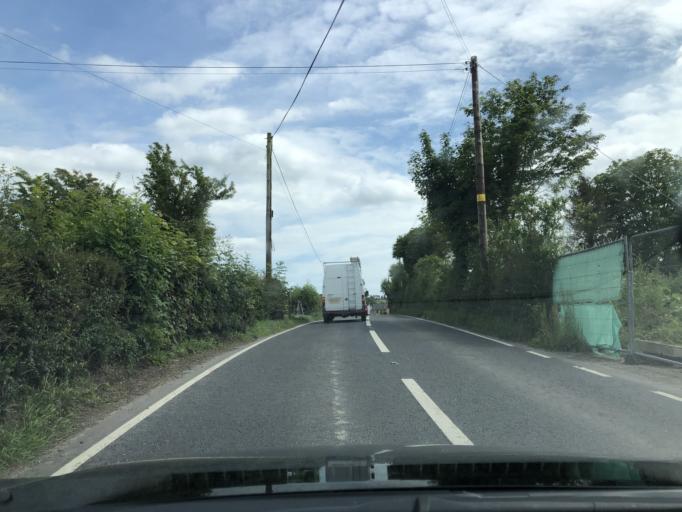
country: GB
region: Northern Ireland
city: Ballynahinch
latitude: 54.4146
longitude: -5.9055
